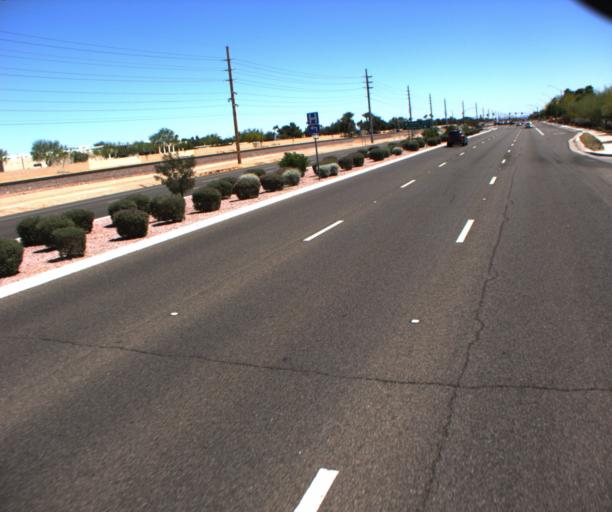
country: US
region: Arizona
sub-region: Maricopa County
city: Sun City West
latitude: 33.6591
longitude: -112.3767
